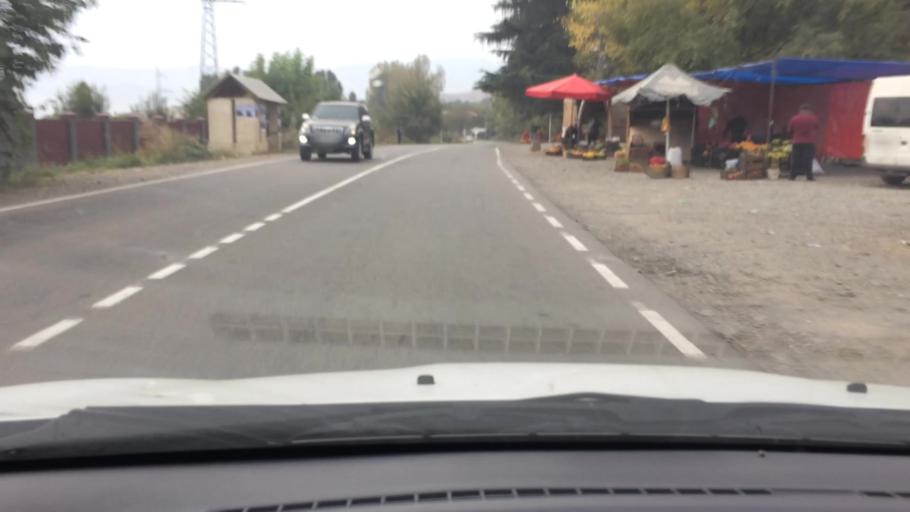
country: AM
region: Tavush
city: Bagratashen
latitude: 41.2957
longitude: 44.7888
